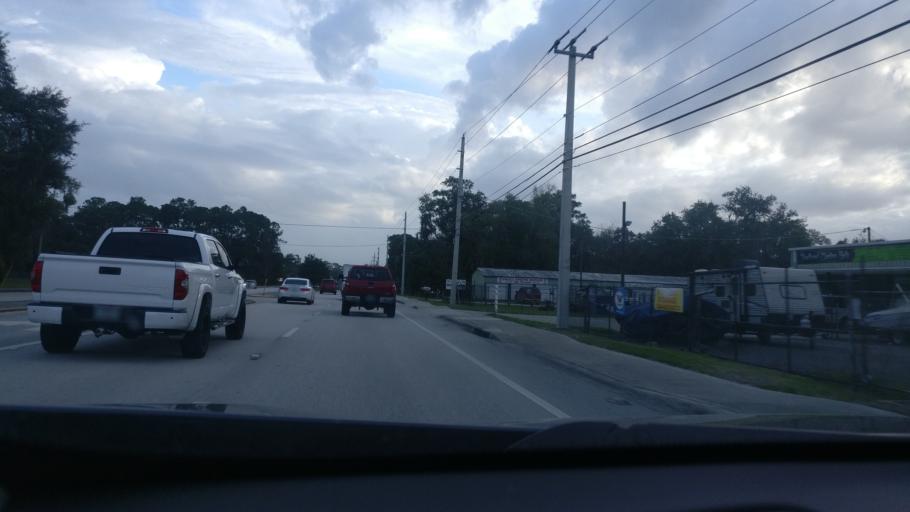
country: US
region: Florida
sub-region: Volusia County
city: DeBary
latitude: 28.8490
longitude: -81.3223
